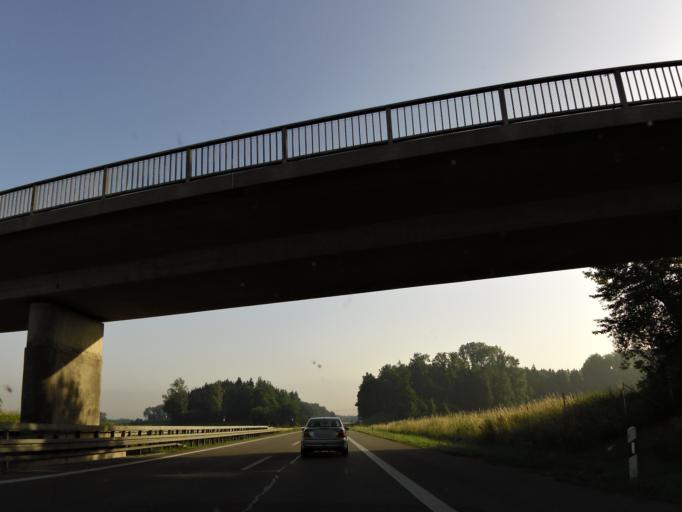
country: DE
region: Bavaria
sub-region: Swabia
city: Holzheim
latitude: 48.3823
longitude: 10.0857
